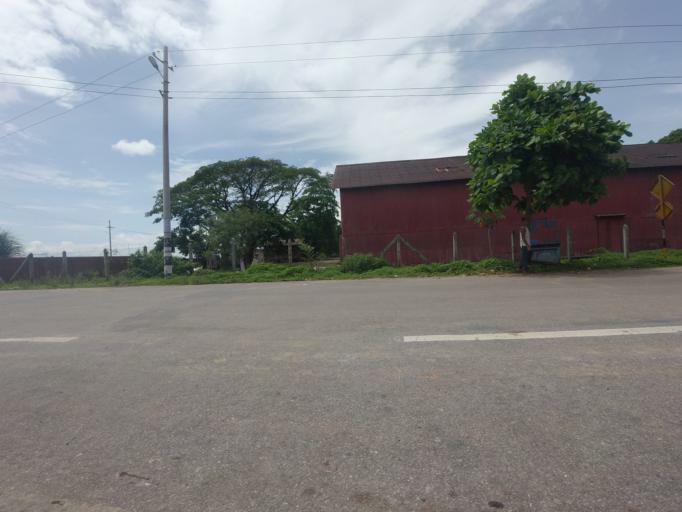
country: MM
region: Mon
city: Mawlamyine
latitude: 16.4516
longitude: 97.6231
